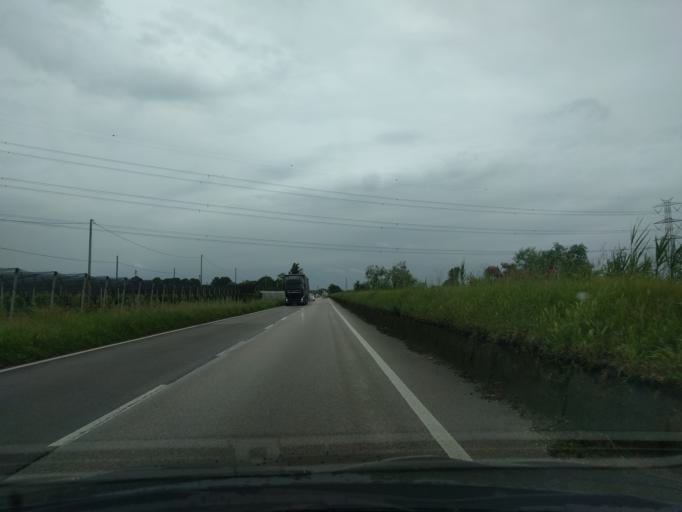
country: IT
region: Veneto
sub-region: Provincia di Rovigo
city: Bottrighe
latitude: 45.0518
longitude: 12.1206
